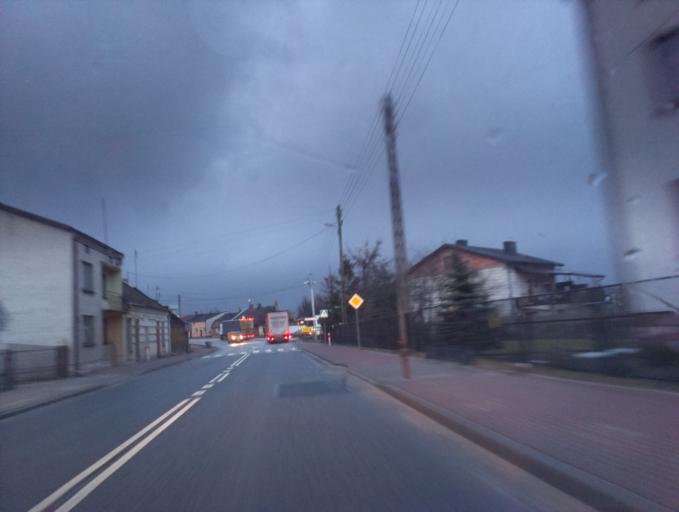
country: PL
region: Lodz Voivodeship
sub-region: Powiat opoczynski
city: Zarnow
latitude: 51.2451
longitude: 20.1749
